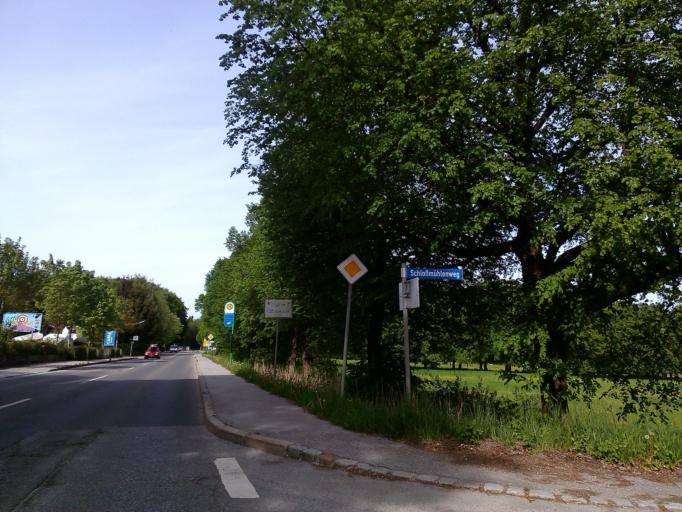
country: DE
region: Bavaria
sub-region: Upper Bavaria
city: Tutzing
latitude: 47.9225
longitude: 11.2893
